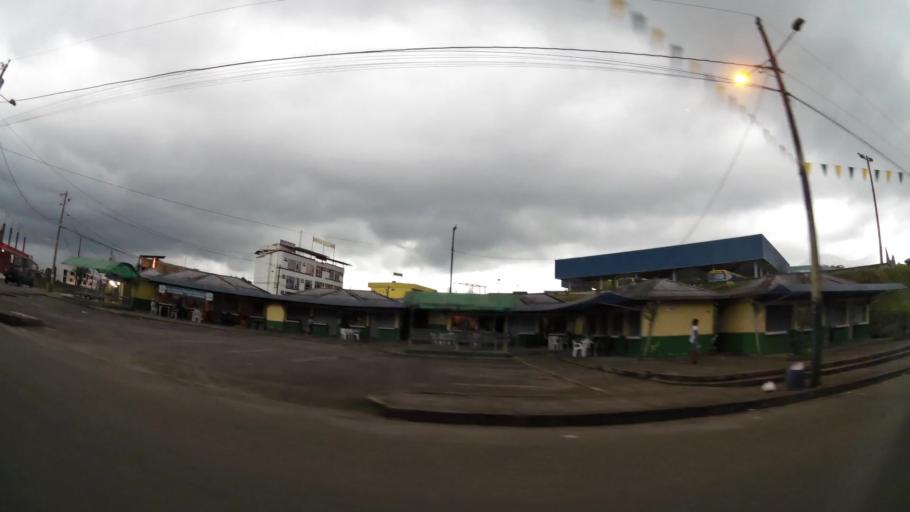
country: EC
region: Pastaza
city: Puyo
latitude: -1.4894
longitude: -78.0061
